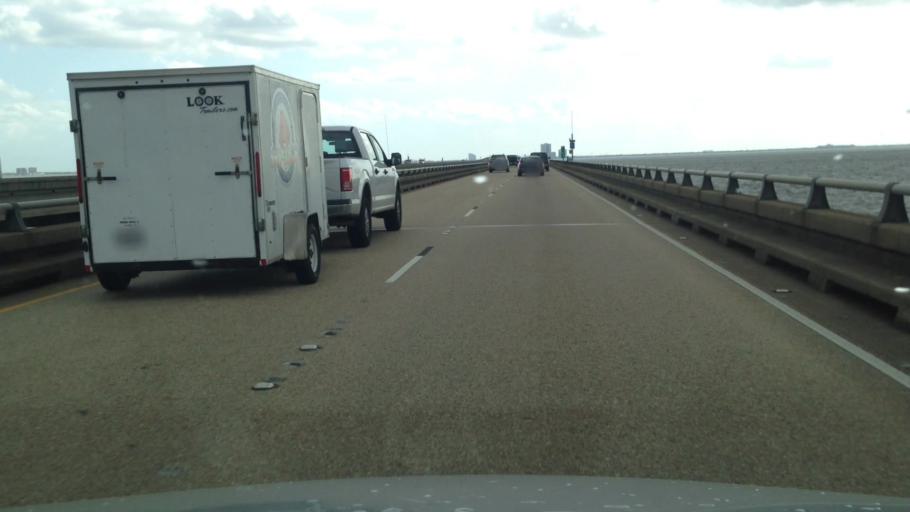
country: US
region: Louisiana
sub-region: Jefferson Parish
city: Metairie
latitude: 30.0860
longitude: -90.1429
